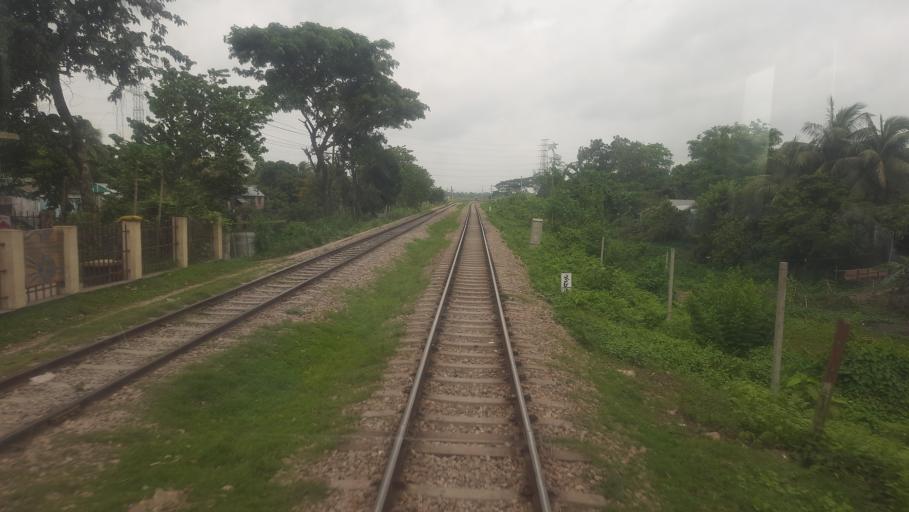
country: BD
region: Dhaka
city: Bhairab Bazar
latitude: 23.9671
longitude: 91.0965
